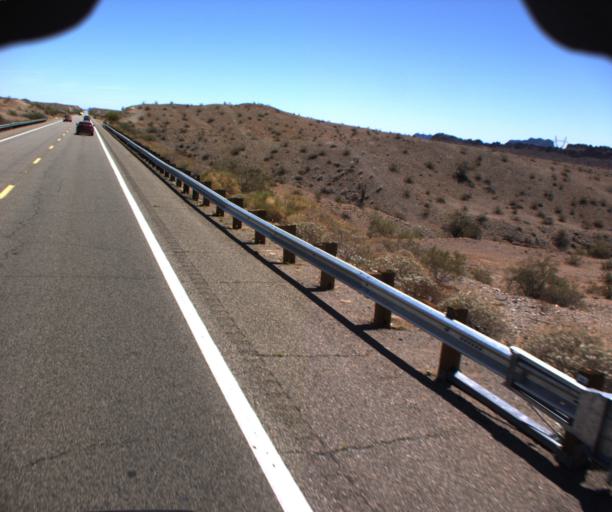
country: US
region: Arizona
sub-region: Mohave County
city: Lake Havasu City
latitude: 34.4413
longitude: -114.2306
